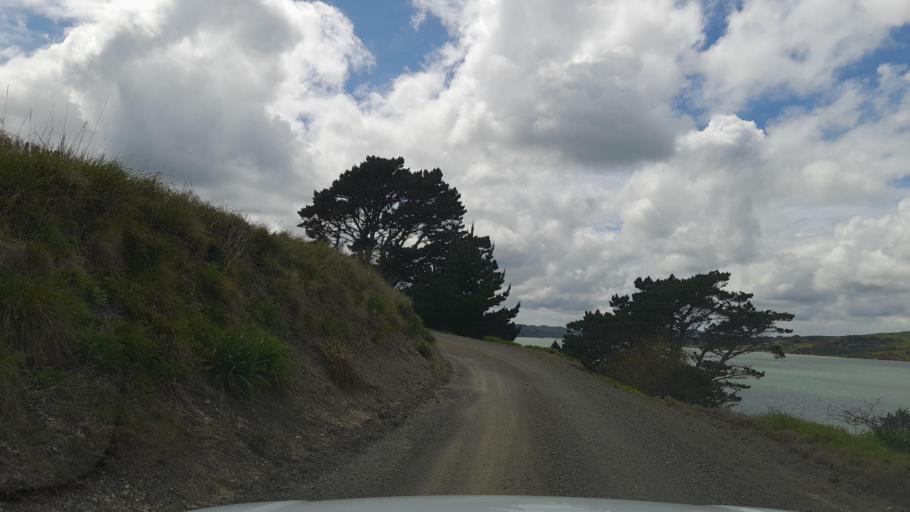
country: NZ
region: Auckland
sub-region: Auckland
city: Wellsford
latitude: -36.2185
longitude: 174.3211
